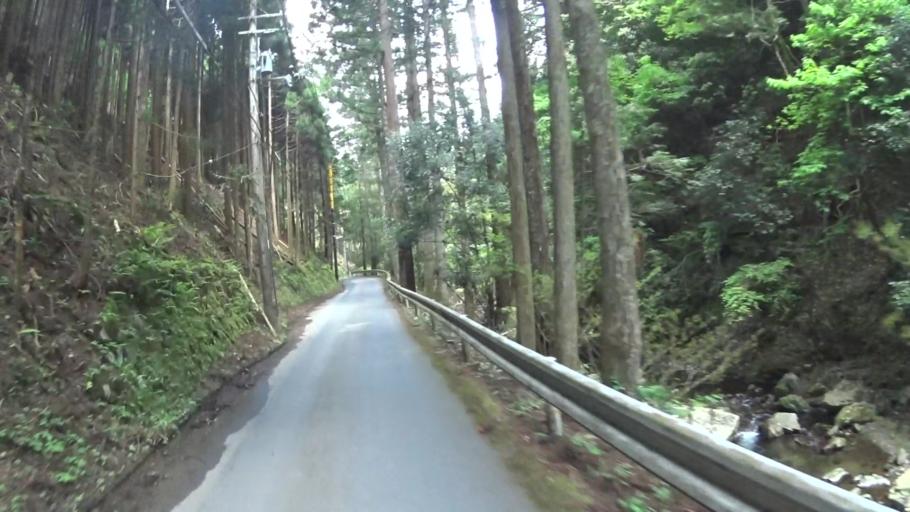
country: JP
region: Kyoto
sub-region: Kyoto-shi
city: Kamigyo-ku
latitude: 35.1021
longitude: 135.7033
